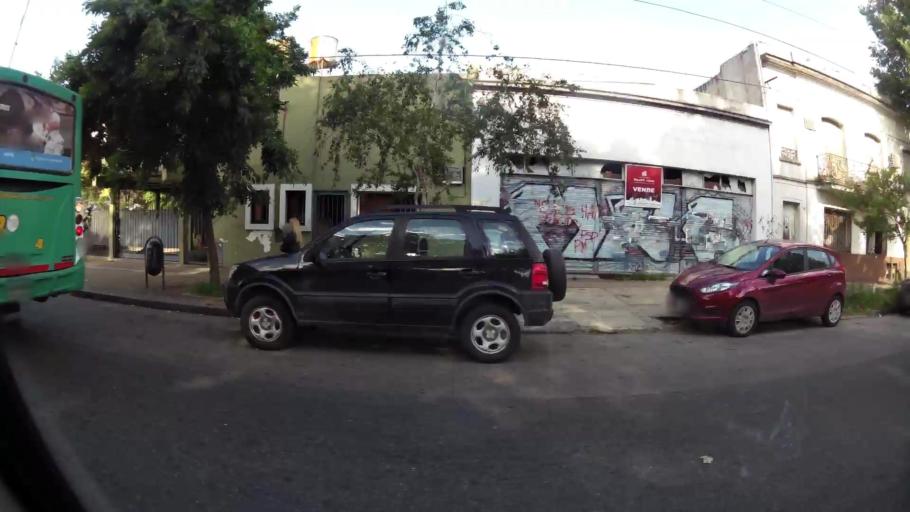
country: AR
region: Buenos Aires
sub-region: Partido de La Plata
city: La Plata
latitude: -34.8966
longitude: -57.9495
